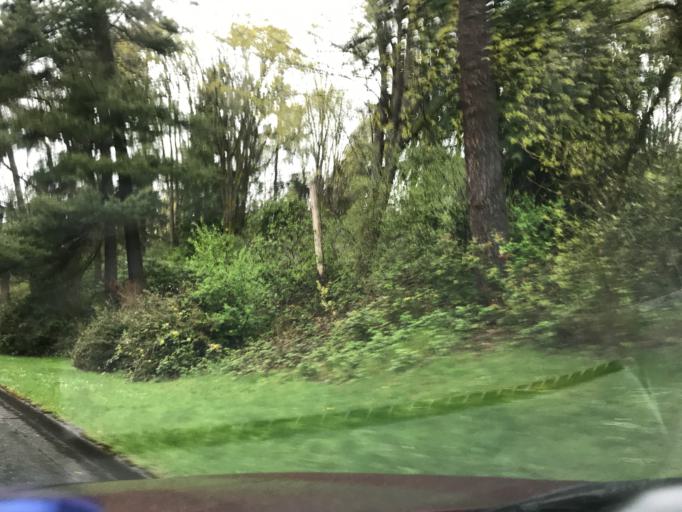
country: US
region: Washington
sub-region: King County
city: Seattle
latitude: 47.6289
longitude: -122.2959
